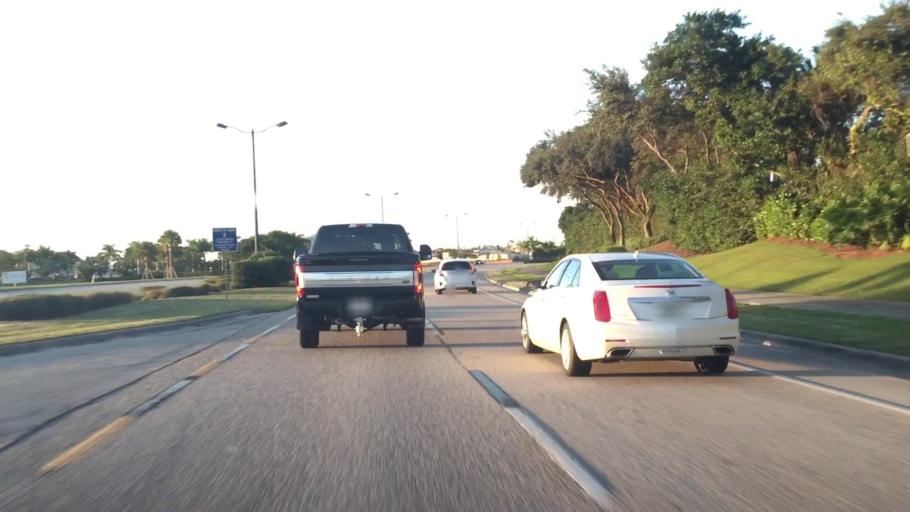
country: US
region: Florida
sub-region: Lee County
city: Three Oaks
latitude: 26.4442
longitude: -81.7735
